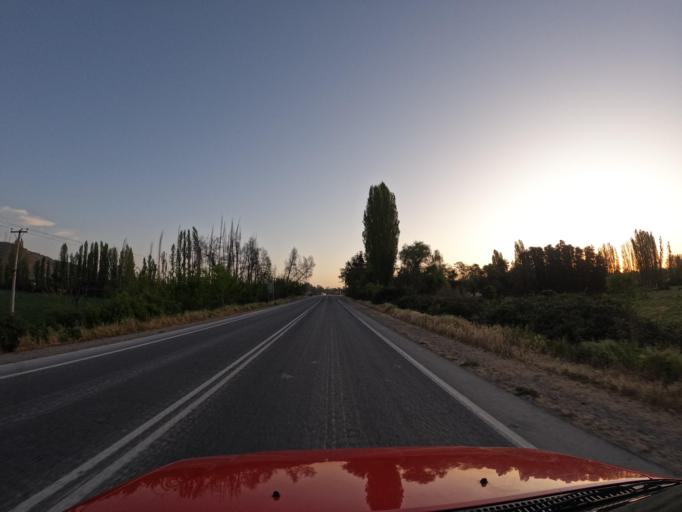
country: CL
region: O'Higgins
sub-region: Provincia de Cachapoal
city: San Vicente
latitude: -34.1638
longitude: -71.3942
